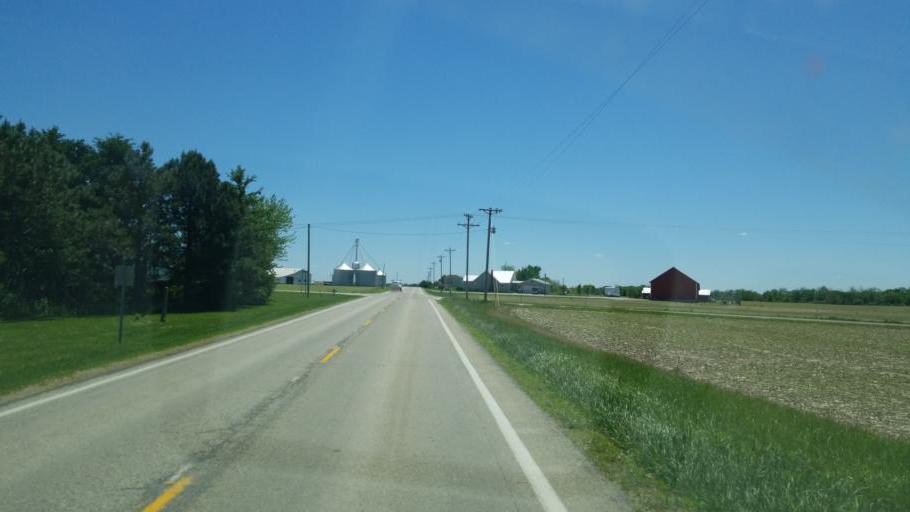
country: US
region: Ohio
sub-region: Darke County
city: Ansonia
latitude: 40.2657
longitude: -84.7008
